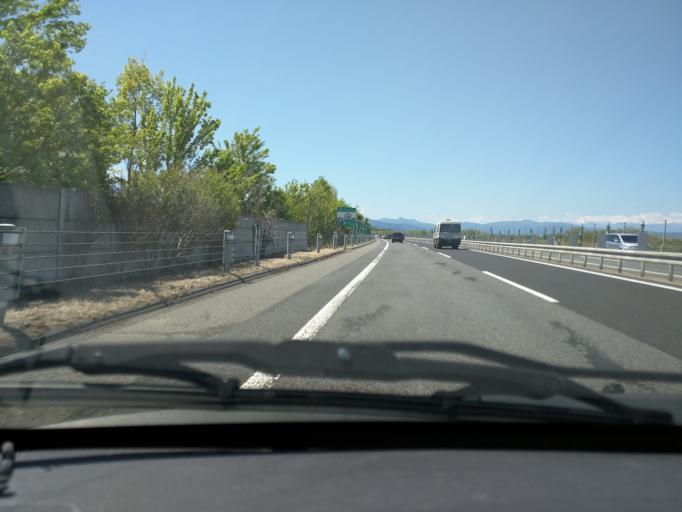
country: JP
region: Nagano
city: Suzaka
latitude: 36.7007
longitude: 138.3000
